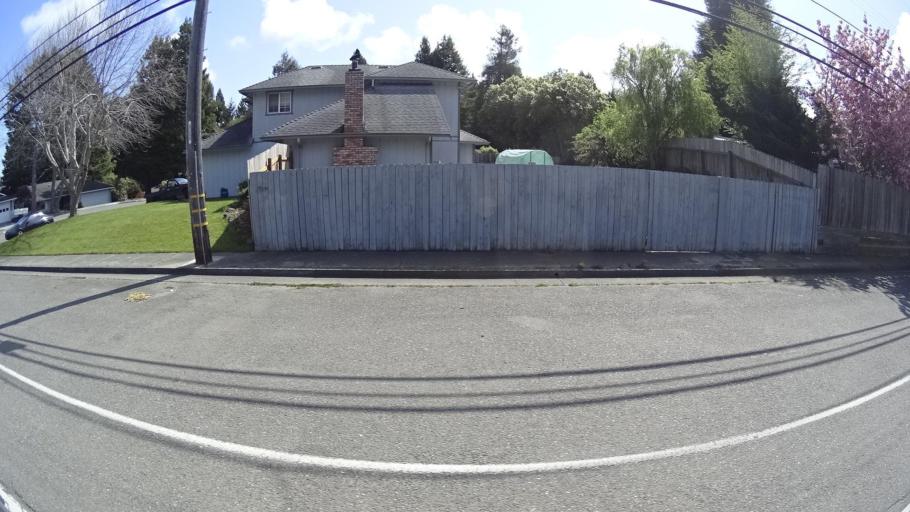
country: US
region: California
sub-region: Humboldt County
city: Pine Hills
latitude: 40.7420
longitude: -124.1474
